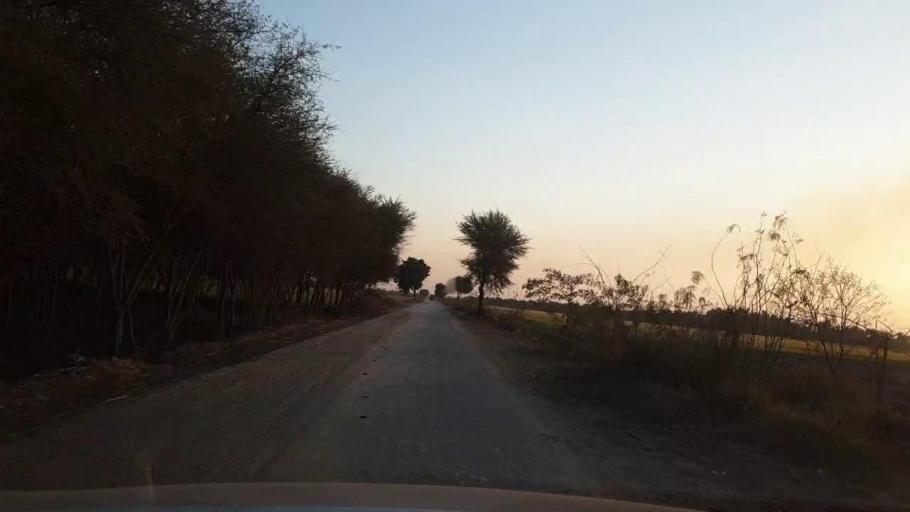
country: PK
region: Sindh
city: Tando Allahyar
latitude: 25.5360
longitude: 68.6278
